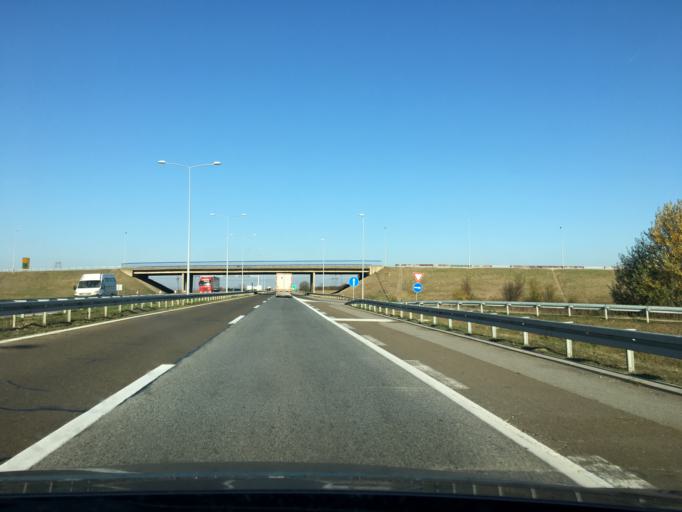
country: RS
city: Novi Karlovci
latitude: 45.0708
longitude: 20.1507
